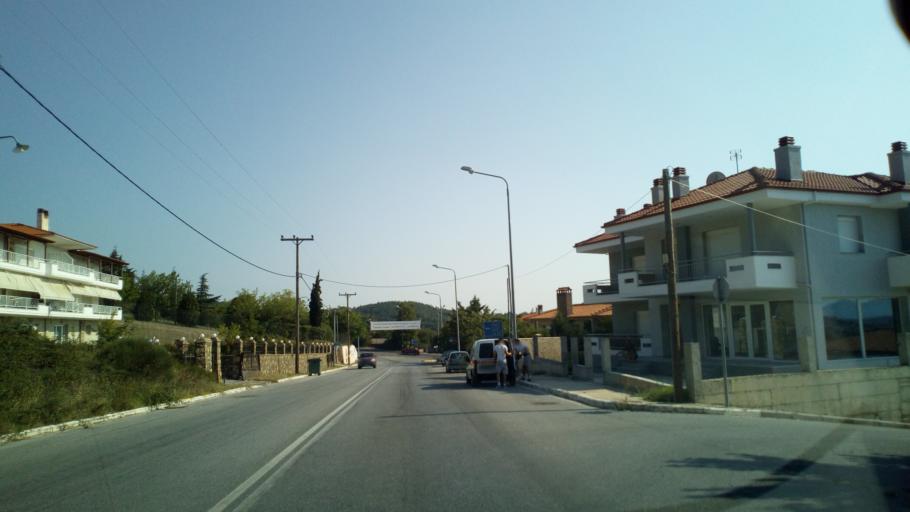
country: GR
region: Central Macedonia
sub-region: Nomos Chalkidikis
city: Polygyros
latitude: 40.3766
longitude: 23.4515
